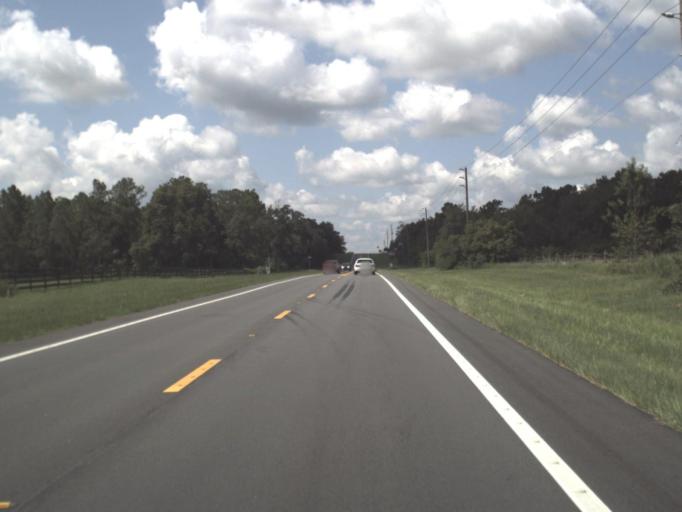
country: US
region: Florida
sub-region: Citrus County
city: Floral City
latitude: 28.7043
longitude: -82.3138
